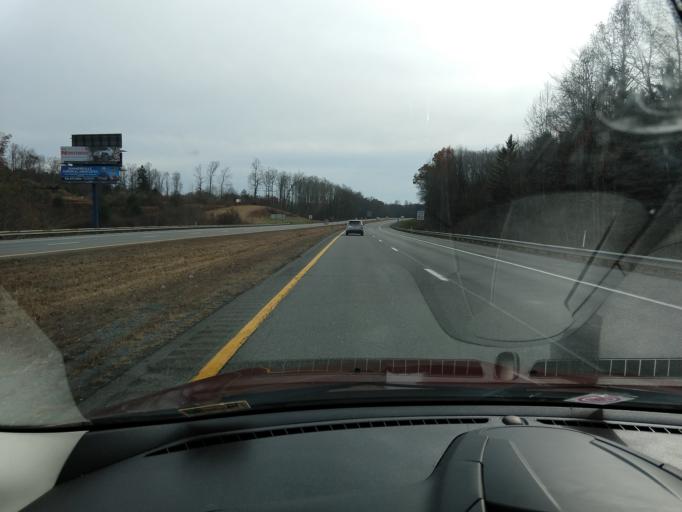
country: US
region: West Virginia
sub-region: Nicholas County
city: Summersville
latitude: 38.2905
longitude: -80.8325
